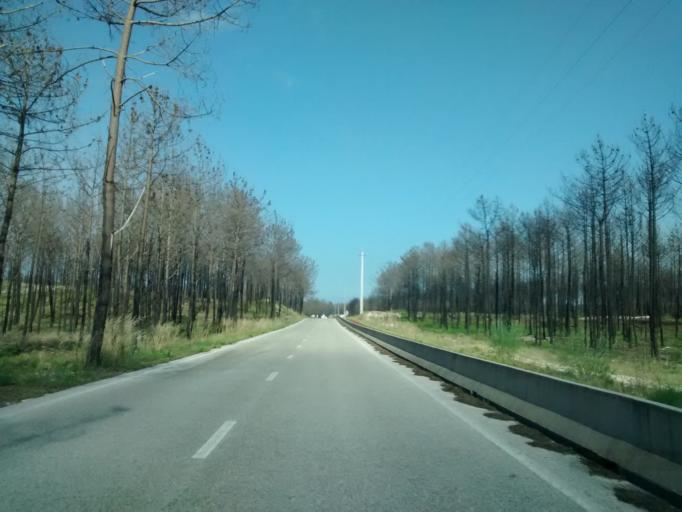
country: PT
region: Coimbra
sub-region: Figueira da Foz
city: Lavos
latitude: 40.0011
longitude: -8.8719
